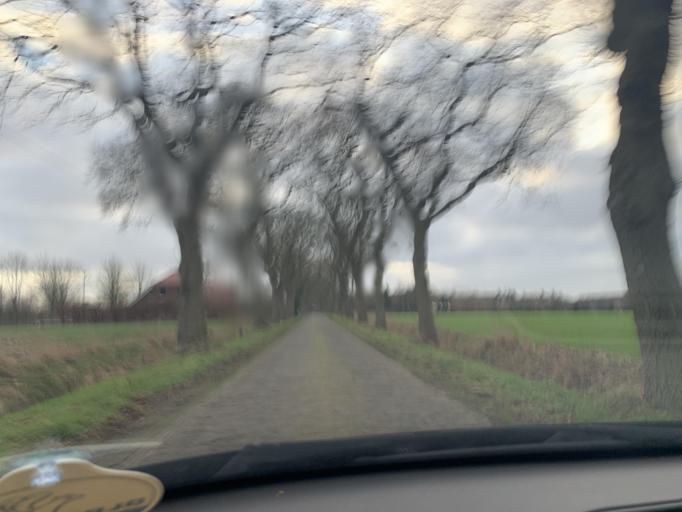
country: DE
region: Lower Saxony
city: Westerstede
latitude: 53.2961
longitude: 7.9285
